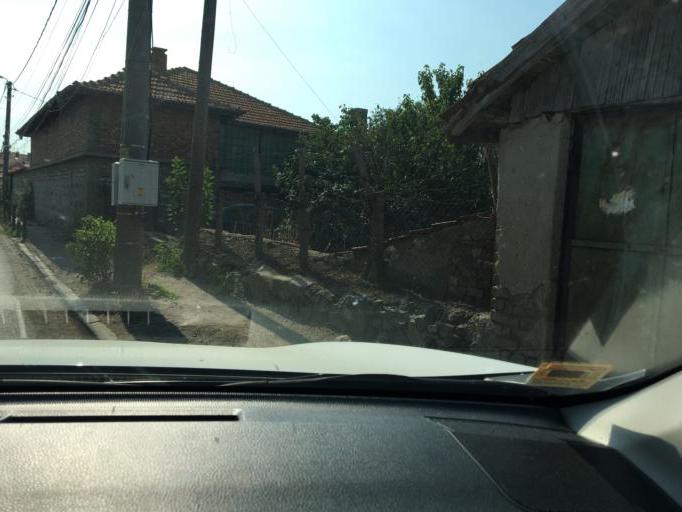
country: BG
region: Burgas
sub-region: Obshtina Burgas
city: Burgas
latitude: 42.6152
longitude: 27.4870
